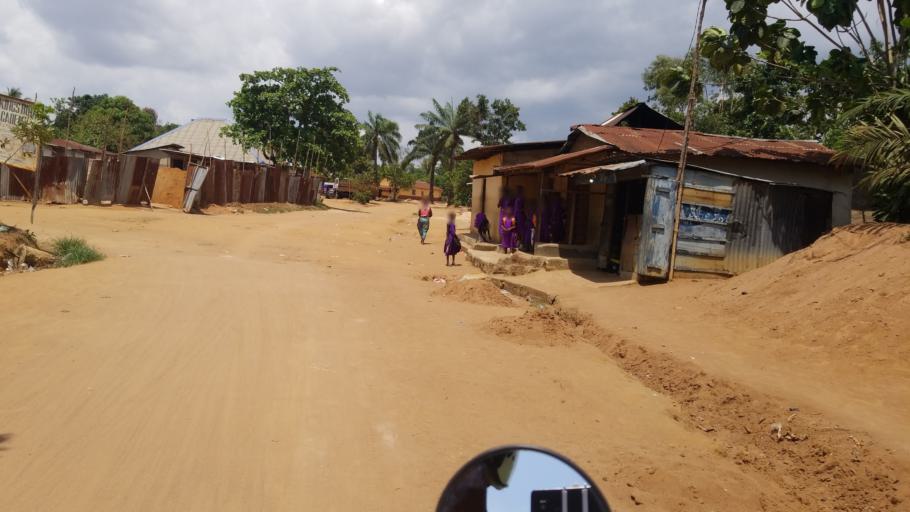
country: SL
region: Western Area
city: Waterloo
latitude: 8.3298
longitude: -13.0597
